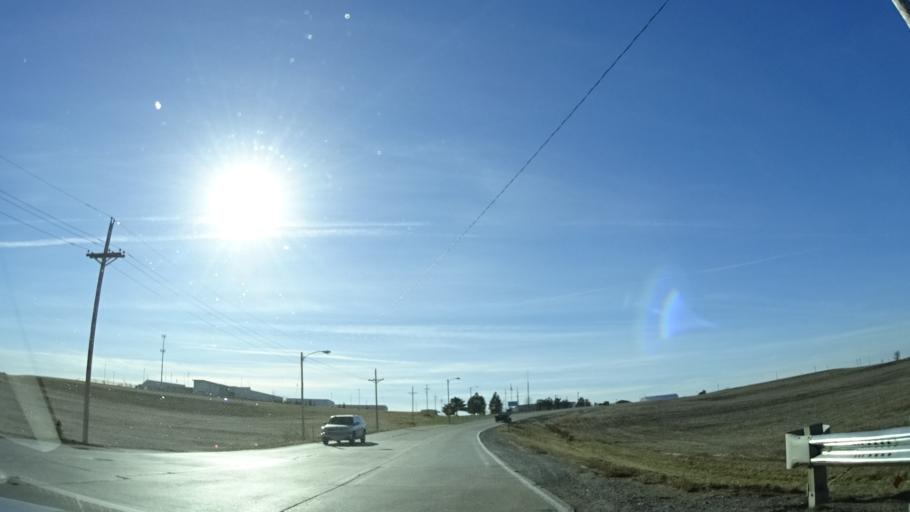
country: US
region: Nebraska
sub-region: Sarpy County
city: Papillion
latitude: 41.0924
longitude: -96.0431
